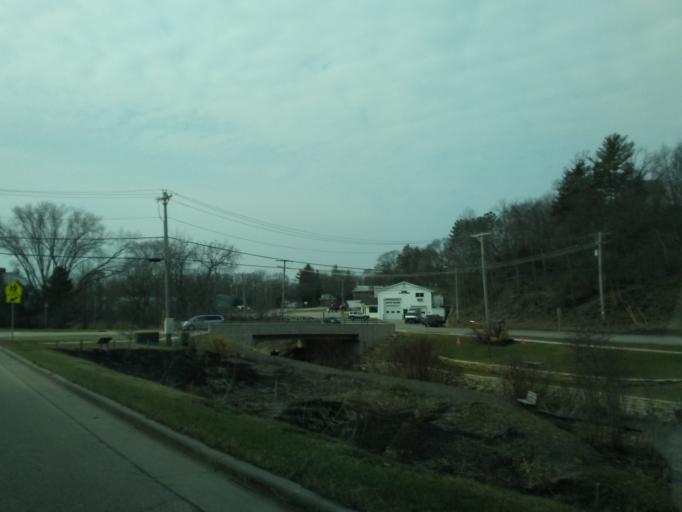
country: US
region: Wisconsin
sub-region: Columbia County
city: Lodi
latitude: 43.3107
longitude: -89.5259
